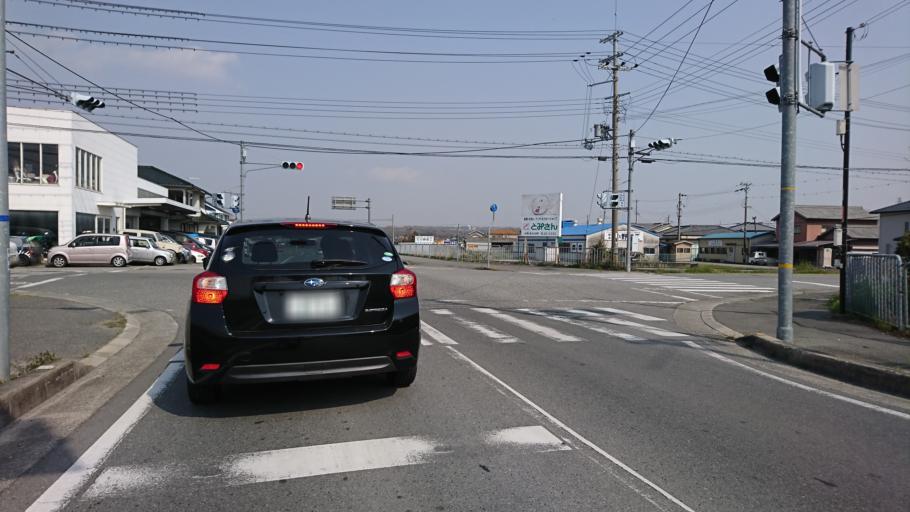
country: JP
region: Hyogo
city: Ono
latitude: 34.8384
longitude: 134.9233
